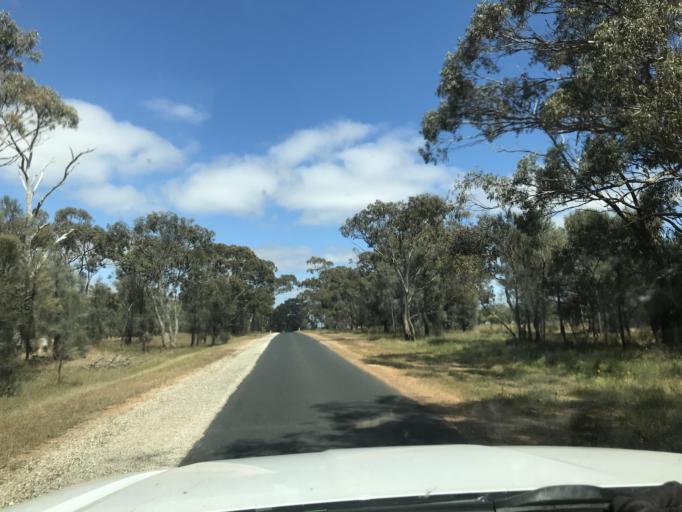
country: AU
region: South Australia
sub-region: Tatiara
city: Bordertown
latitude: -36.3064
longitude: 141.0642
